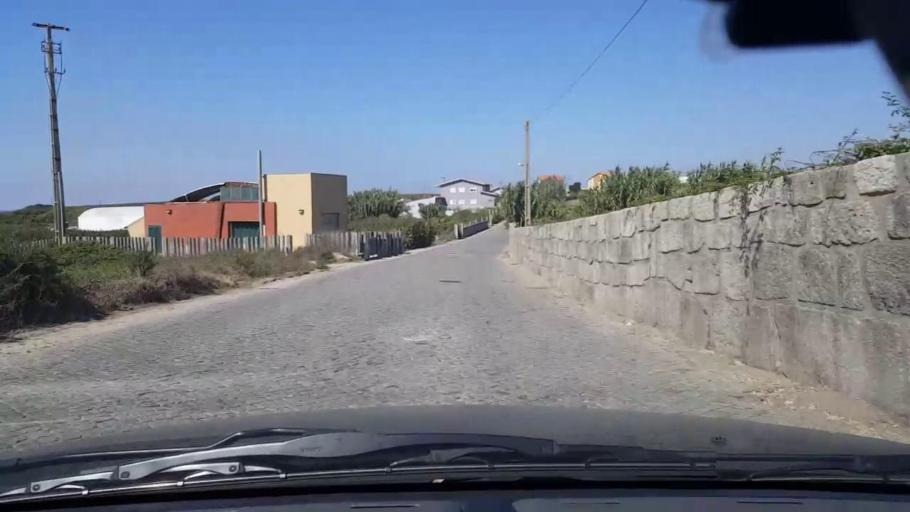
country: PT
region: Porto
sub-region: Matosinhos
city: Lavra
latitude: 41.2868
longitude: -8.7256
